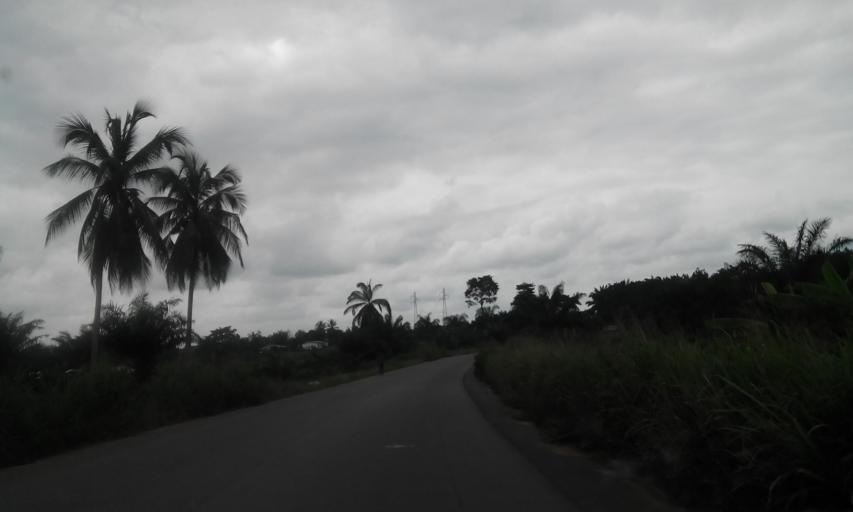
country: CI
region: Sud-Comoe
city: Adiake
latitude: 5.4015
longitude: -3.3849
